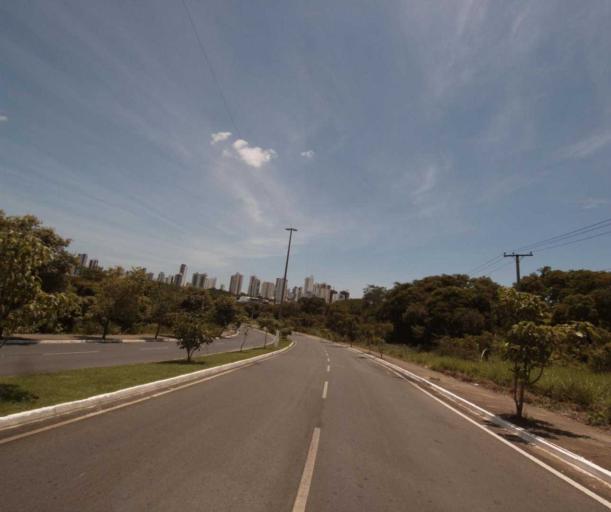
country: BR
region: Mato Grosso
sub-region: Cuiaba
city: Cuiaba
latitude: -15.5708
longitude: -56.1078
